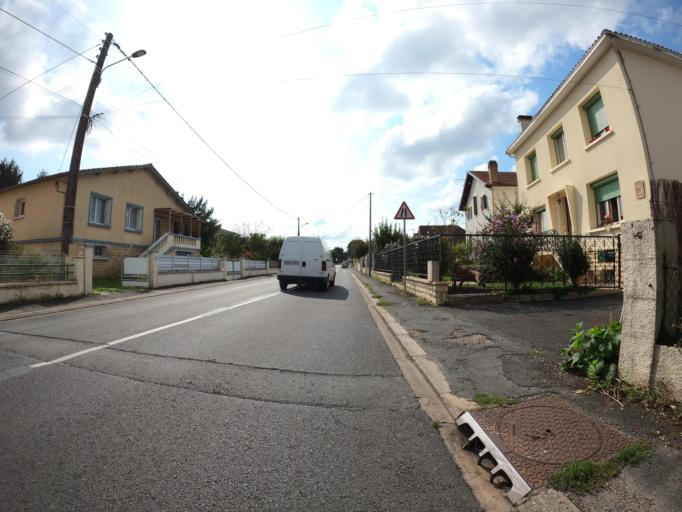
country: FR
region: Aquitaine
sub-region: Departement de la Dordogne
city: Bergerac
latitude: 44.8413
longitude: 0.4831
